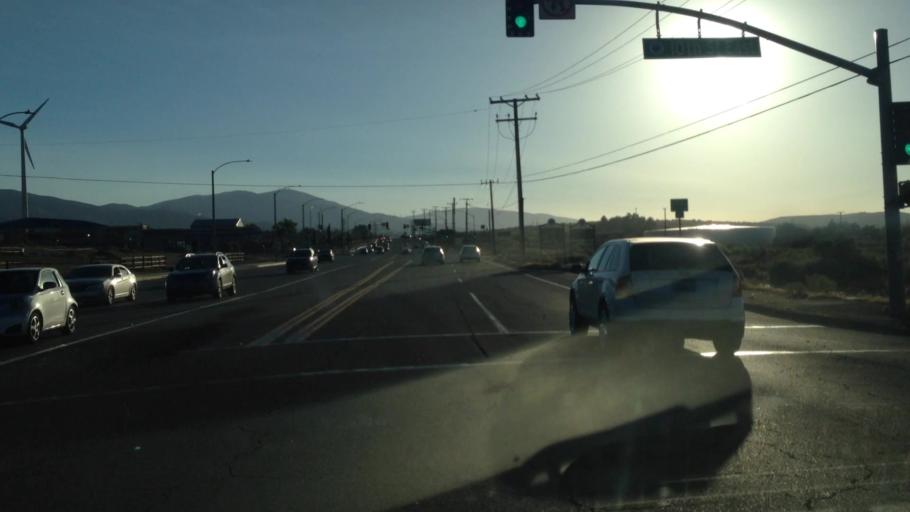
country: US
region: California
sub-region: Los Angeles County
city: Palmdale
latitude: 34.5578
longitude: -118.1114
